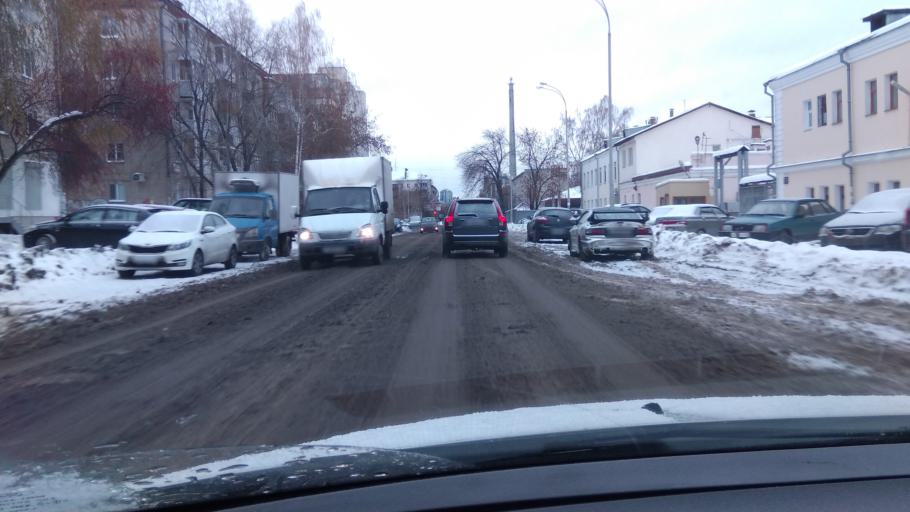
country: RU
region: Sverdlovsk
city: Yekaterinburg
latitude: 56.8115
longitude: 60.6121
